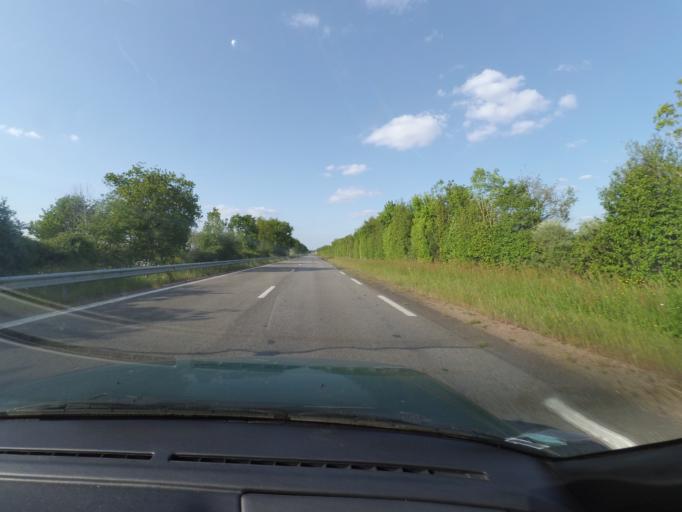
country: FR
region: Pays de la Loire
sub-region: Departement de la Vendee
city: Saligny
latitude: 46.8501
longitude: -1.4128
